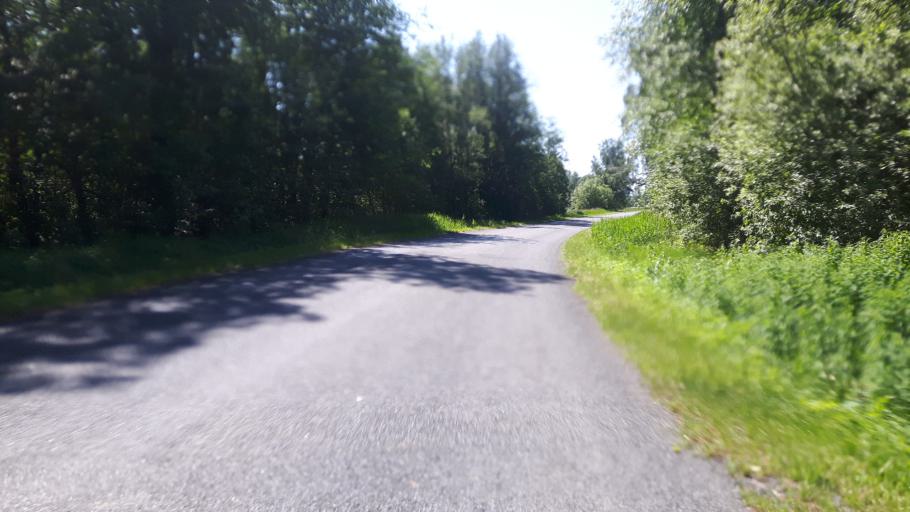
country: EE
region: Paernumaa
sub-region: Vaendra vald (alev)
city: Vandra
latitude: 58.5793
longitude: 25.0000
